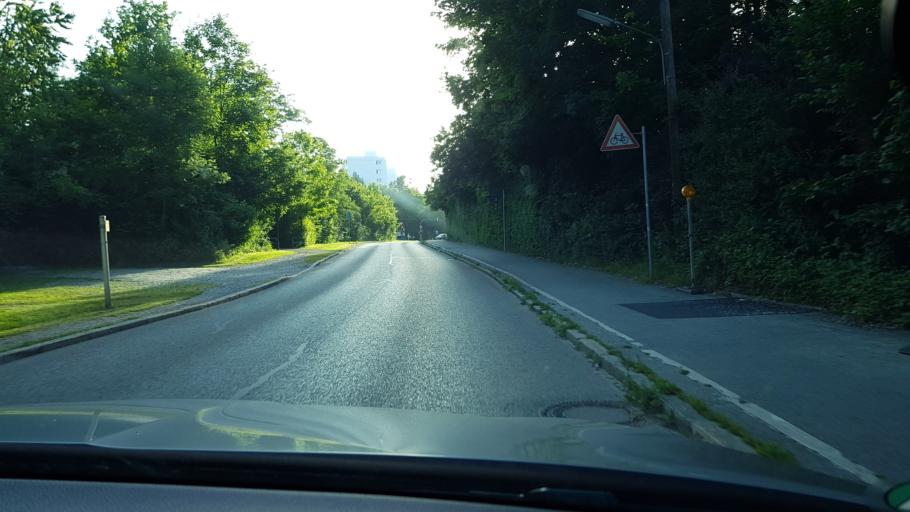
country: DE
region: Bavaria
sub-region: Upper Bavaria
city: Unterfoehring
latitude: 48.1624
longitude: 11.6478
